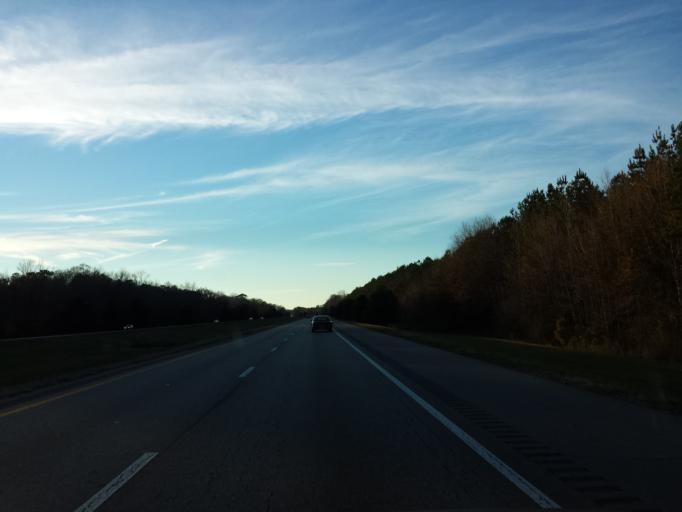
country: US
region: Mississippi
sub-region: Lauderdale County
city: Marion
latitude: 32.4113
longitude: -88.4788
